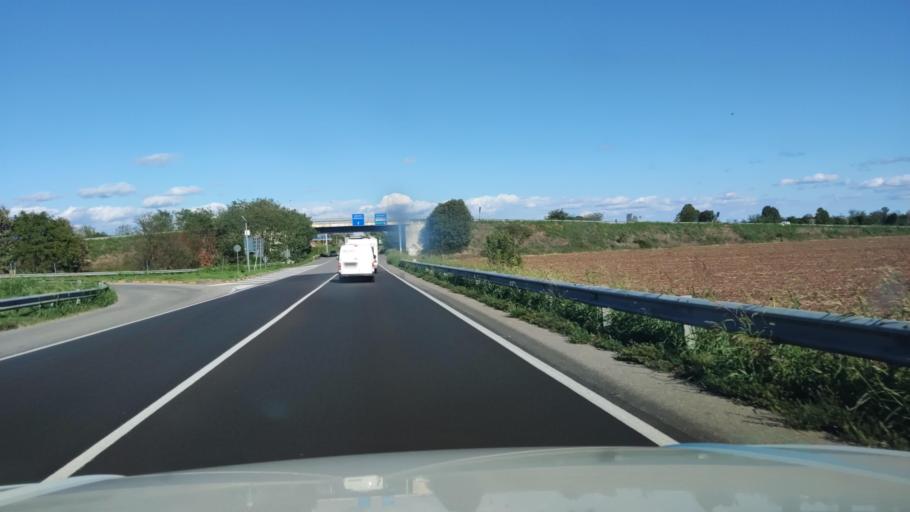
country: IT
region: Lombardy
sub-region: Provincia di Cremona
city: Soncino
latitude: 45.4089
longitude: 9.8643
